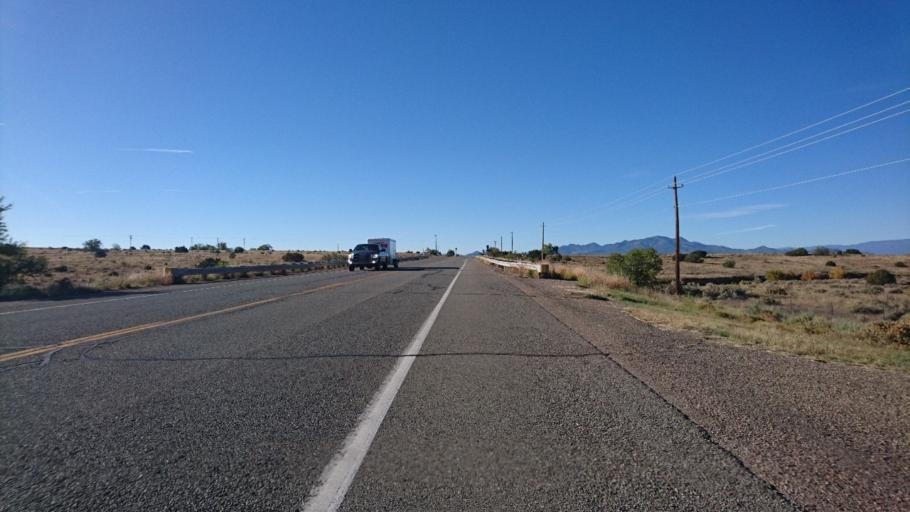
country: US
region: New Mexico
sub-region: Santa Fe County
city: La Cienega
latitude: 35.4968
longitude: -106.0649
